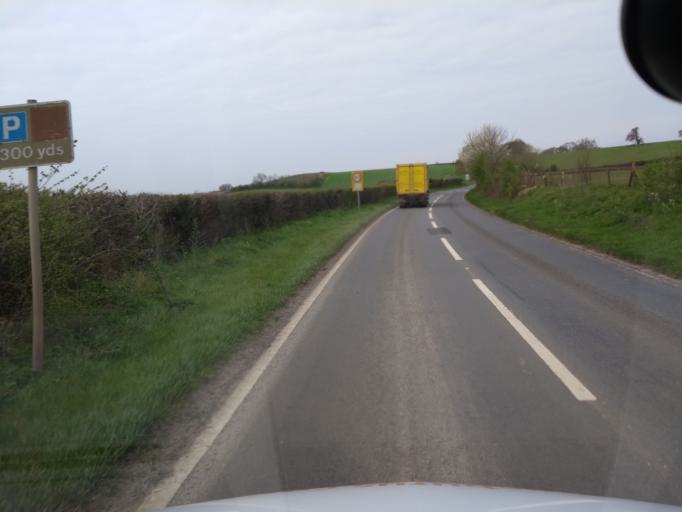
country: GB
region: England
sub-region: Somerset
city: Creech Saint Michael
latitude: 50.9981
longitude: -2.9993
